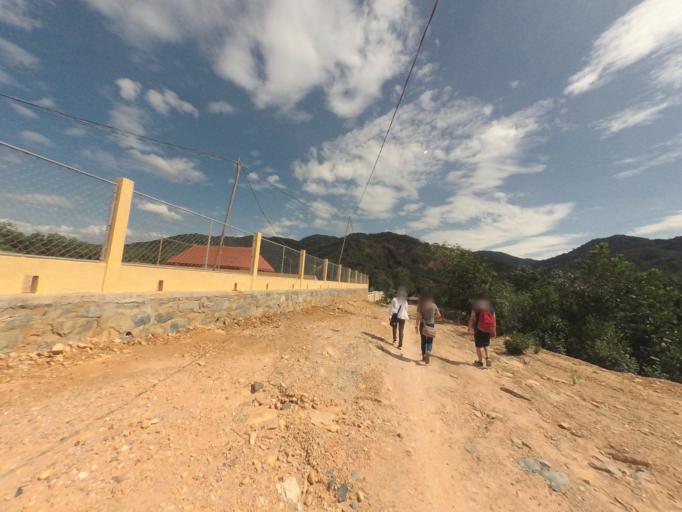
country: VN
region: Thua Thien-Hue
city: A Luoi
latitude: 16.3017
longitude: 107.3250
